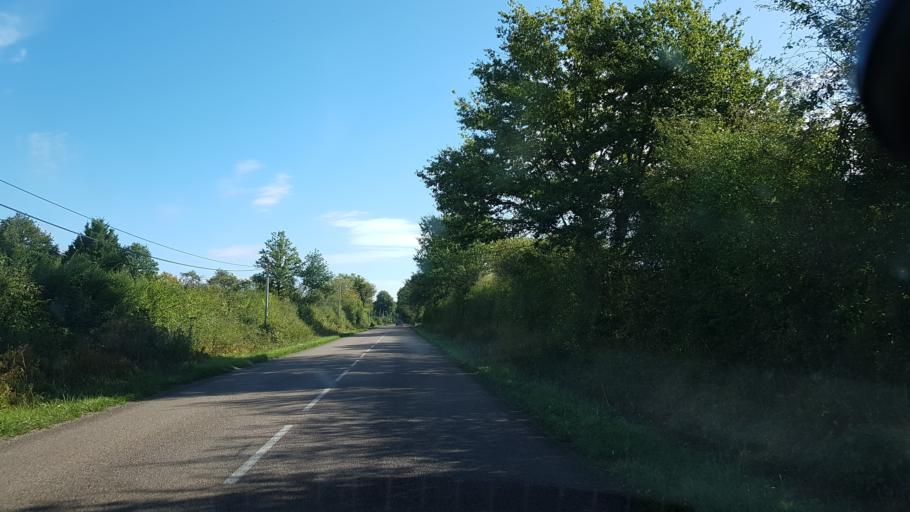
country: FR
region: Bourgogne
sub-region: Departement de la Nievre
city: Saint-Amand-en-Puisaye
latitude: 47.5362
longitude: 3.0794
